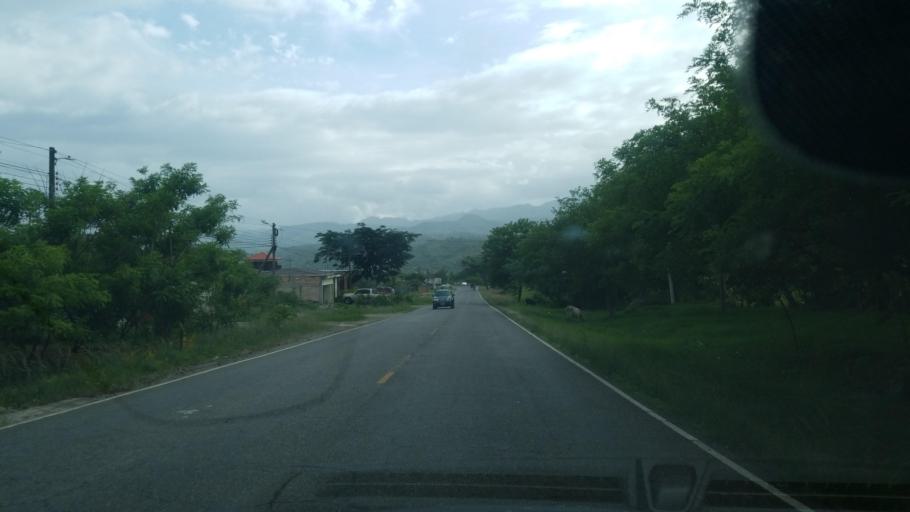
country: HN
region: Ocotepeque
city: Santa Lucia
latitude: 14.4195
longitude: -89.1904
